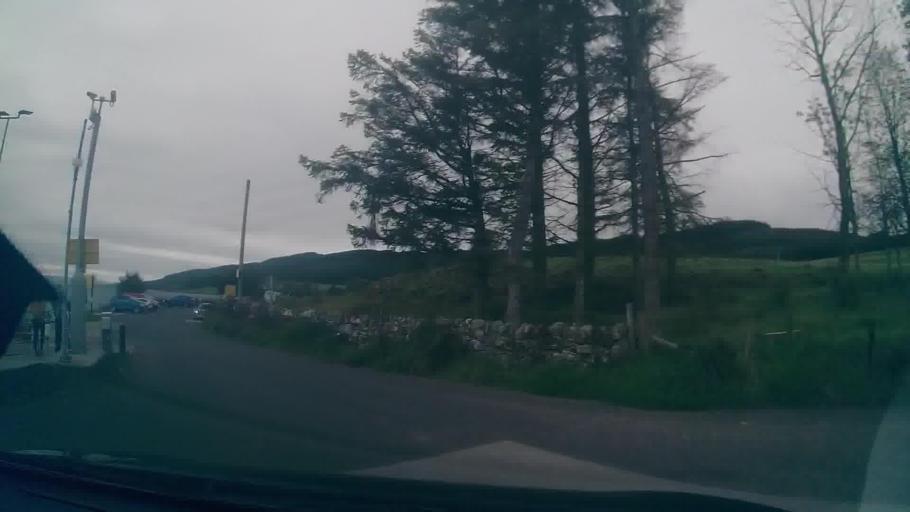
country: GB
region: Scotland
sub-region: Argyll and Bute
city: Port Bannatyne
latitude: 55.9210
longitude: -5.1592
